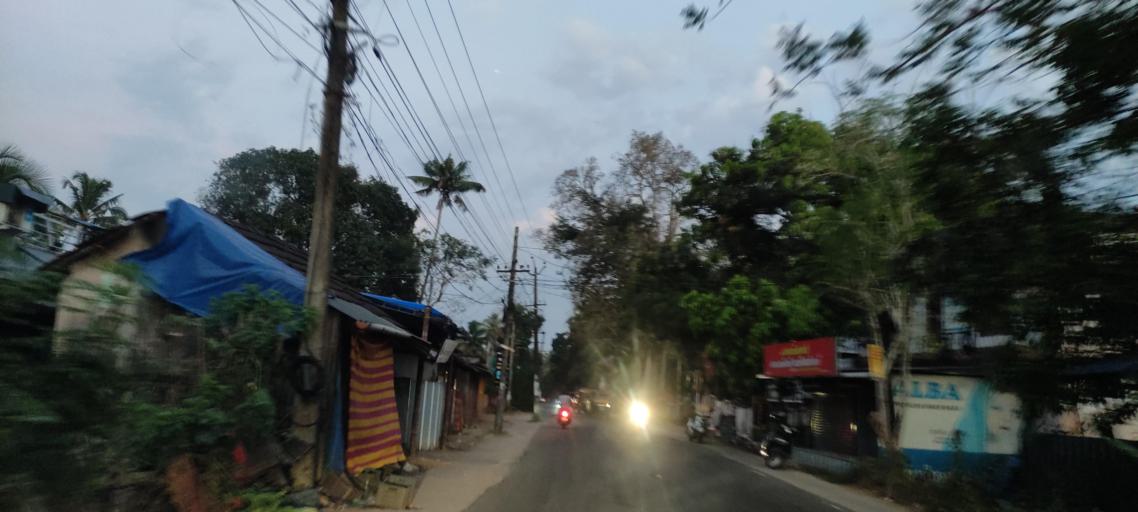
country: IN
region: Kerala
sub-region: Alappuzha
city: Kutiatodu
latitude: 9.7739
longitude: 76.3415
